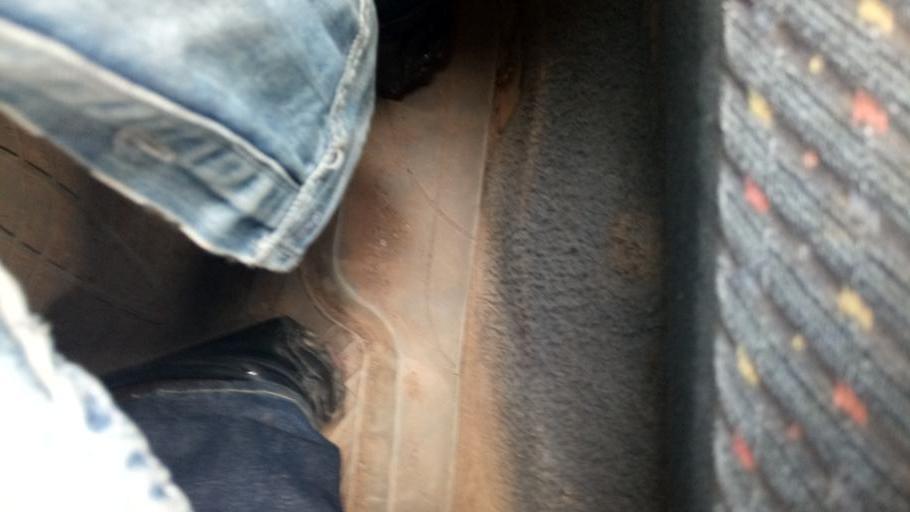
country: CD
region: Katanga
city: Lubumbashi
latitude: -11.6305
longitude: 27.4839
